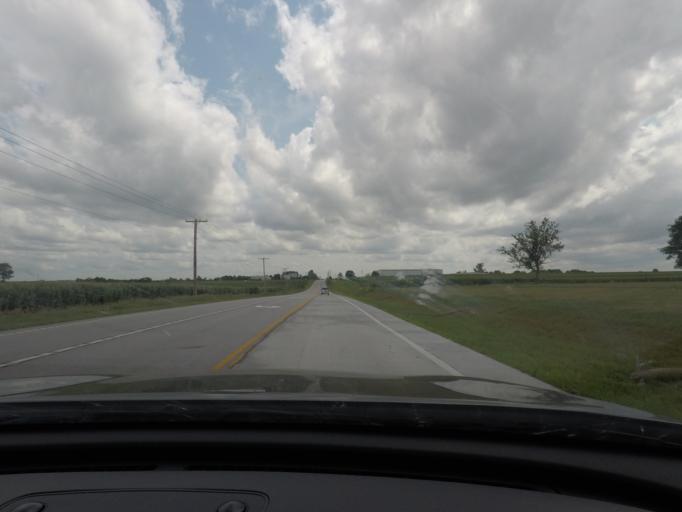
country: US
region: Missouri
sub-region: Lafayette County
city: Higginsville
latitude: 39.0199
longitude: -93.7347
